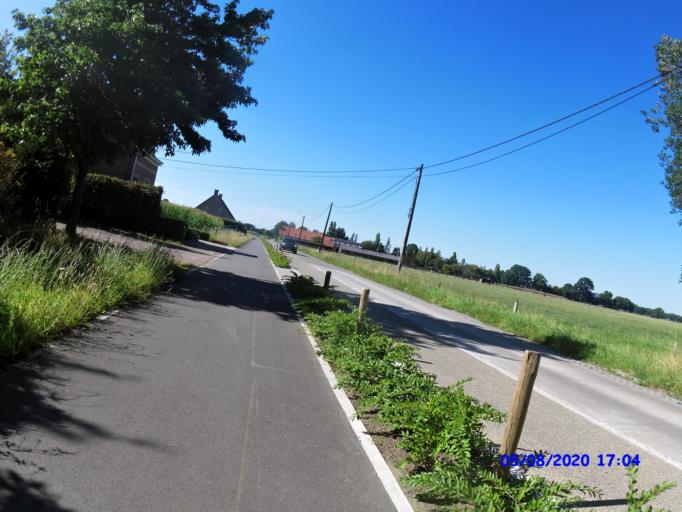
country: BE
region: Flanders
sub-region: Provincie Antwerpen
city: Oostmalle
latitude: 51.3092
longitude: 4.6845
